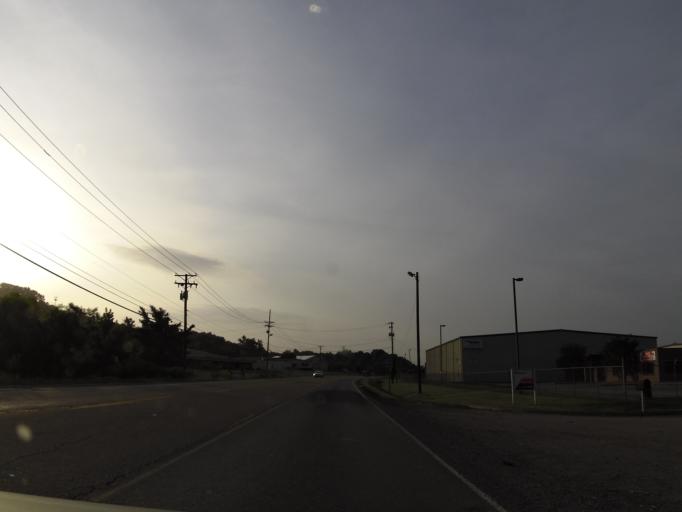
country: US
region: Tennessee
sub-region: Knox County
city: Knoxville
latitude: 35.9631
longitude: -83.8255
